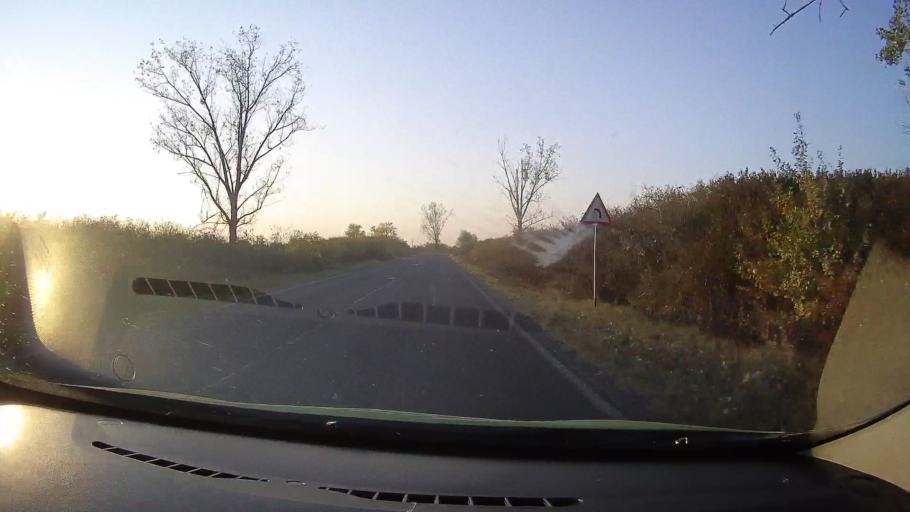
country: RO
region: Arad
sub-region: Comuna Bocsig
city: Bocsig
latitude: 46.4274
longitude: 21.9084
